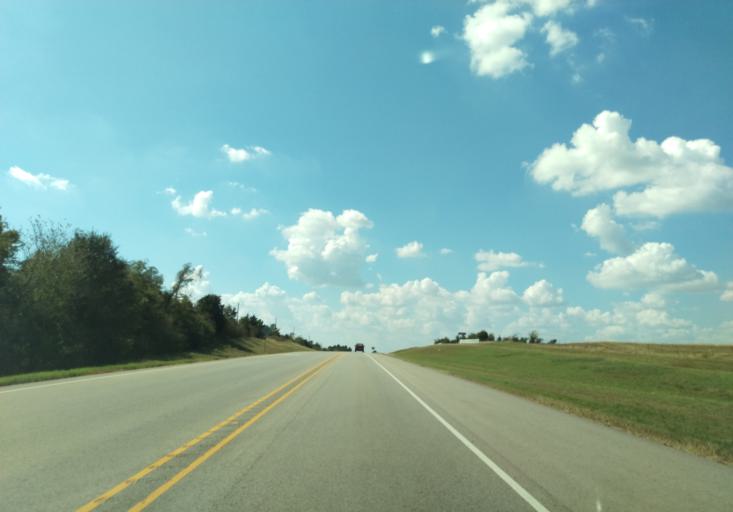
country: US
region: Texas
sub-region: Grimes County
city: Navasota
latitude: 30.3578
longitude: -95.9639
